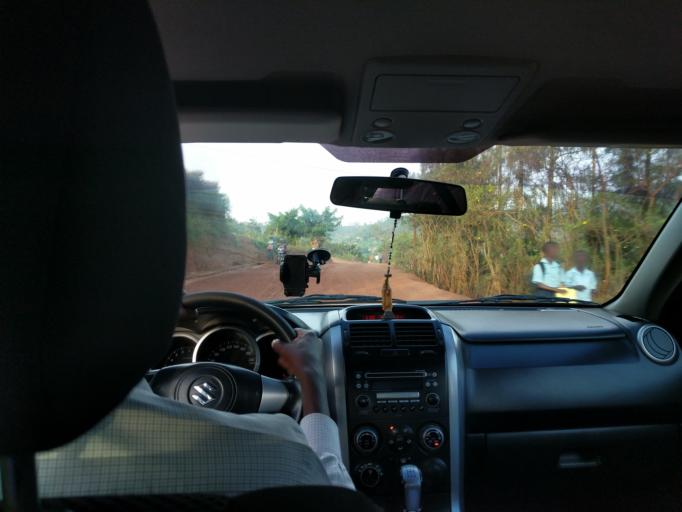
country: RW
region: Kigali
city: Kigali
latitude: -2.0100
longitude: 30.0423
